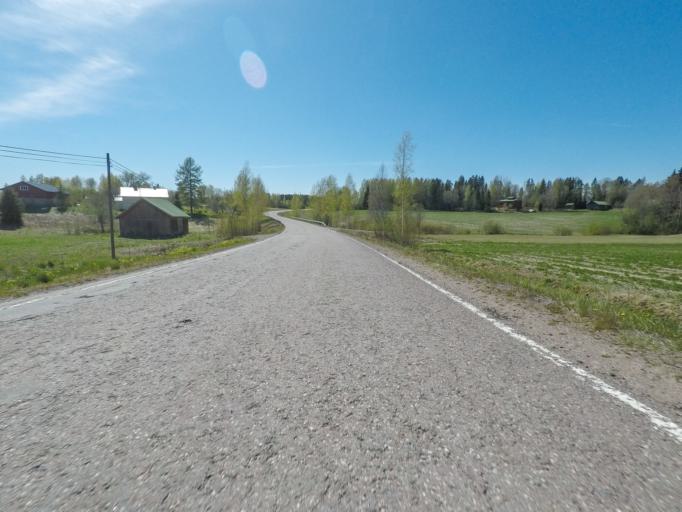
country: FI
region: Uusimaa
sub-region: Helsinki
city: Kaerkoelae
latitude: 60.5843
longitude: 23.7951
